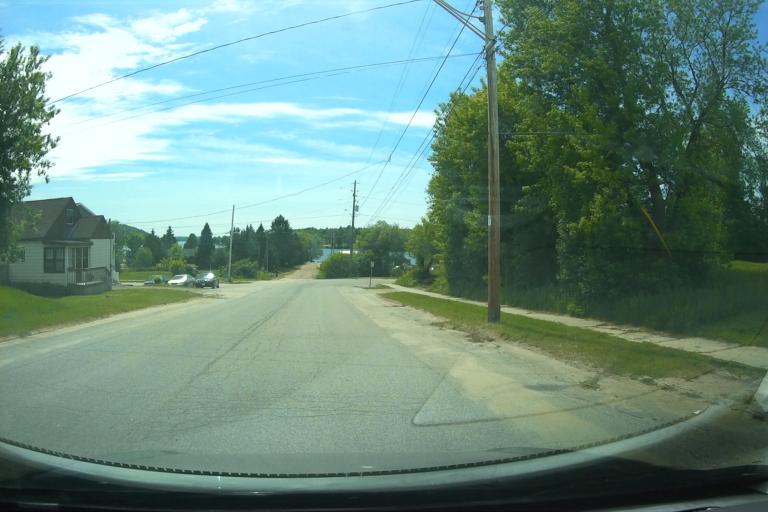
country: CA
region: Ontario
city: Powassan
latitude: 46.2310
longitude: -79.1462
